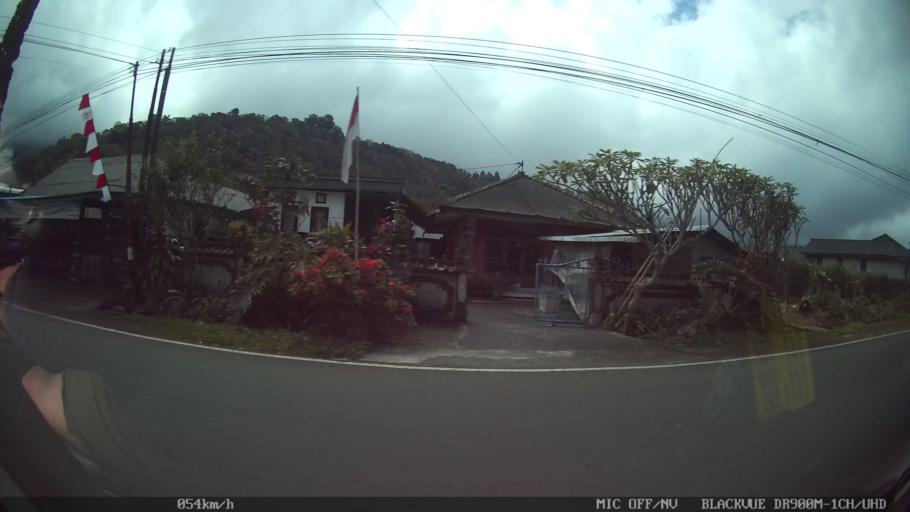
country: ID
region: Bali
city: Munduk
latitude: -8.2591
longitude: 115.1620
